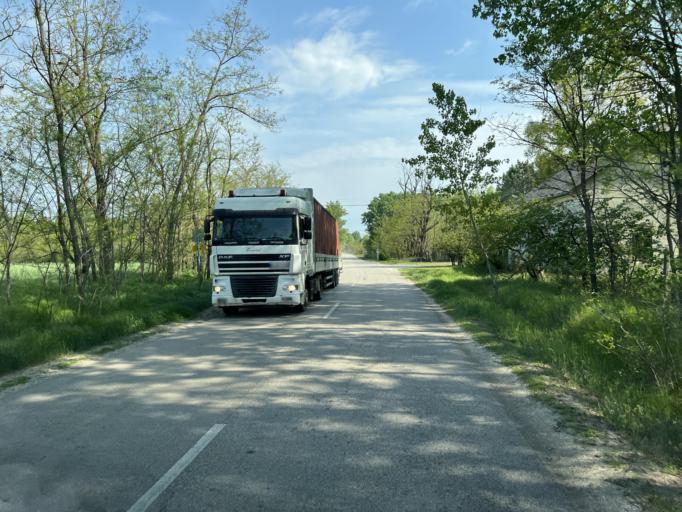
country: HU
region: Pest
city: Kocser
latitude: 47.0207
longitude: 19.9335
